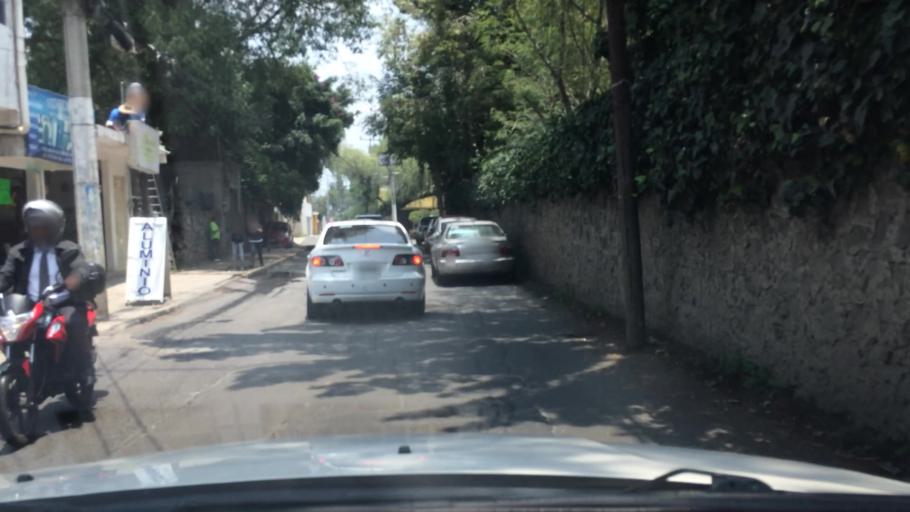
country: MX
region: Mexico City
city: Tlalpan
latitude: 19.2716
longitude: -99.1505
